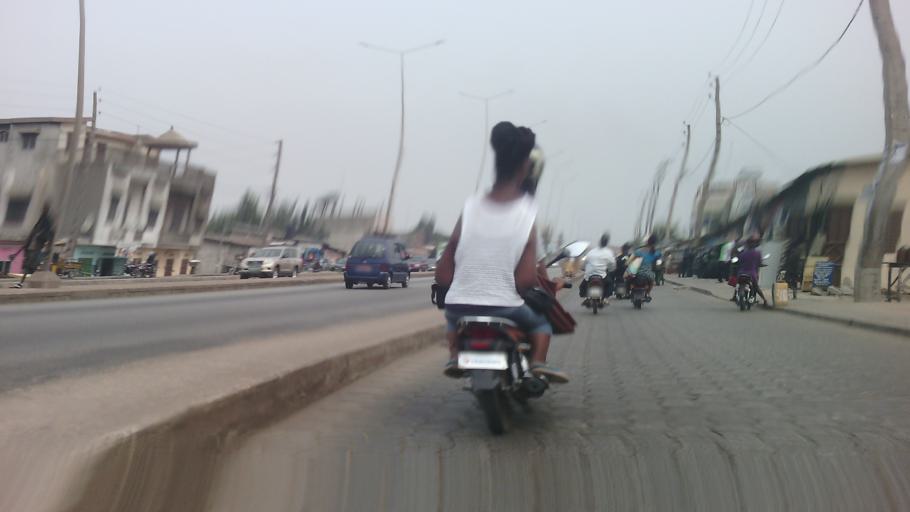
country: BJ
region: Atlantique
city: Abomey-Calavi
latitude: 6.3888
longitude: 2.3607
